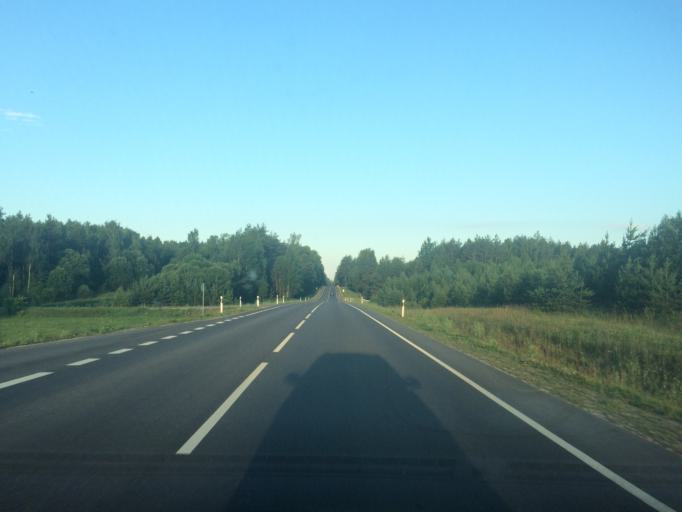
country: LT
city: Zarasai
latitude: 55.7118
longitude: 26.1947
